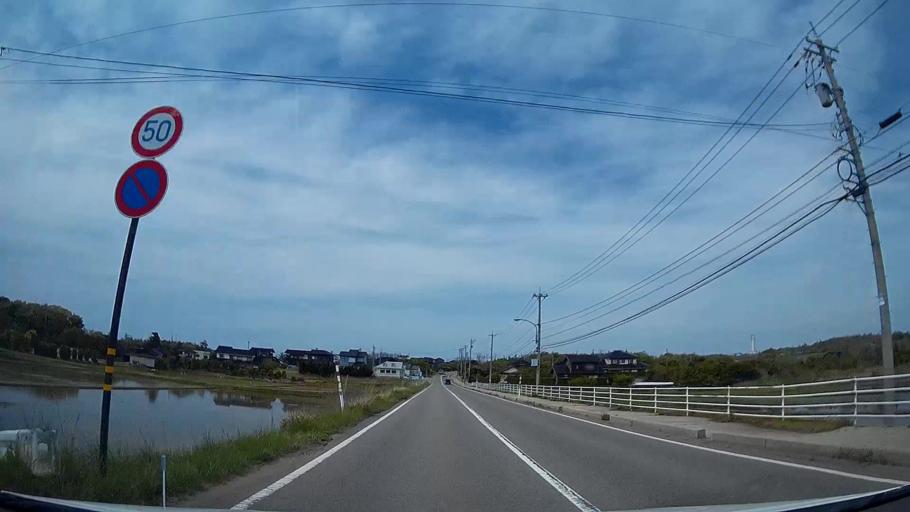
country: JP
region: Ishikawa
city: Hakui
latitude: 36.9829
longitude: 136.7763
